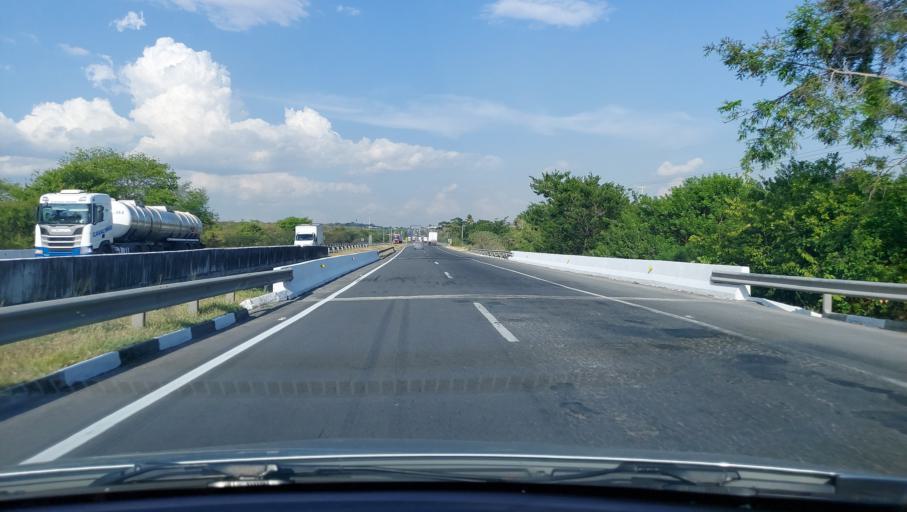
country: BR
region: Bahia
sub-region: Santo Estevao
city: Santo Estevao
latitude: -12.4092
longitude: -39.1810
